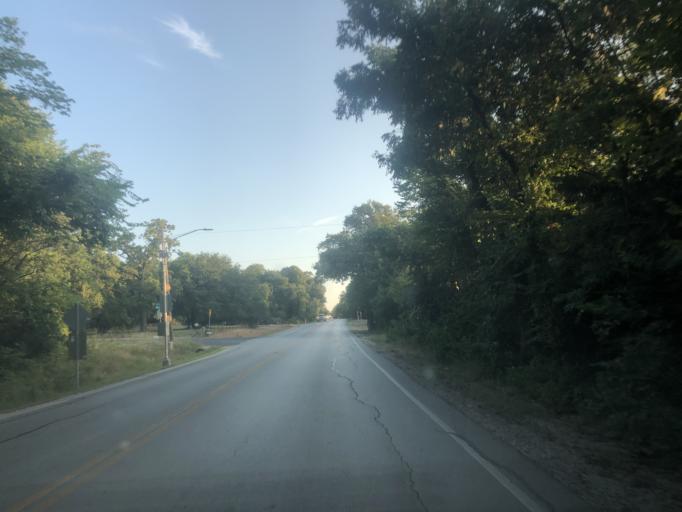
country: US
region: Texas
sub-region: Tarrant County
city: Lakeside
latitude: 32.7947
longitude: -97.4938
